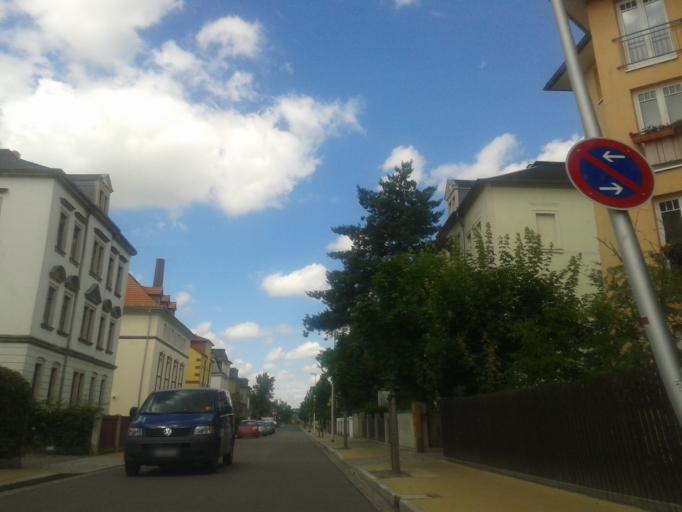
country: DE
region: Saxony
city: Radebeul
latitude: 51.0968
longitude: 13.6804
